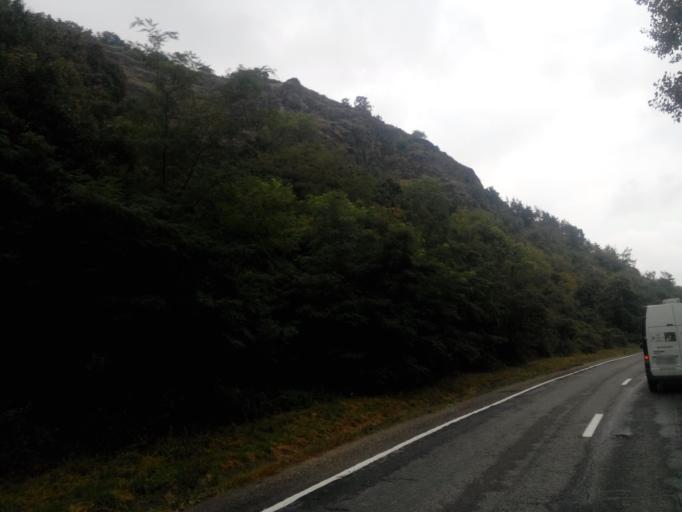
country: RO
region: Cluj
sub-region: Comuna Moldovenesti
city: Moldovenesti
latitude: 46.5094
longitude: 23.6580
